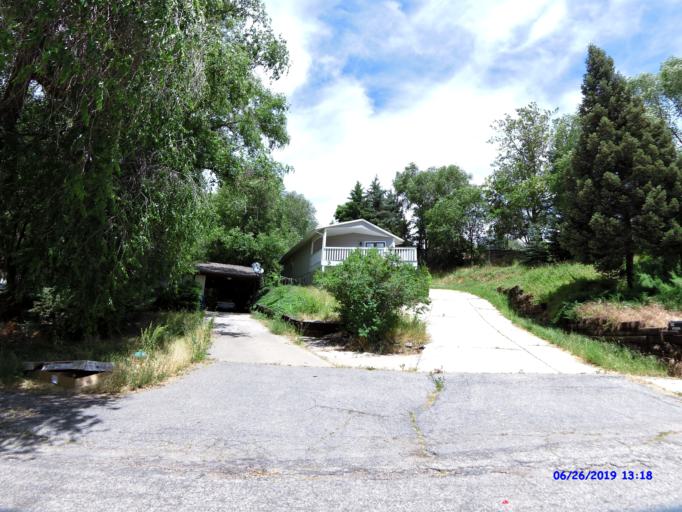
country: US
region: Utah
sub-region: Weber County
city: Ogden
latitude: 41.2090
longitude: -111.9606
